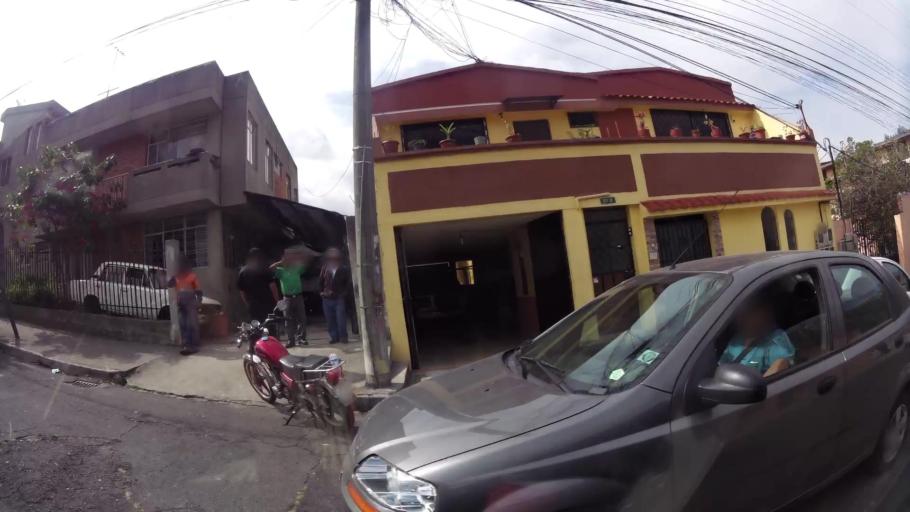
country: EC
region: Pichincha
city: Quito
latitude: -0.2191
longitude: -78.4853
